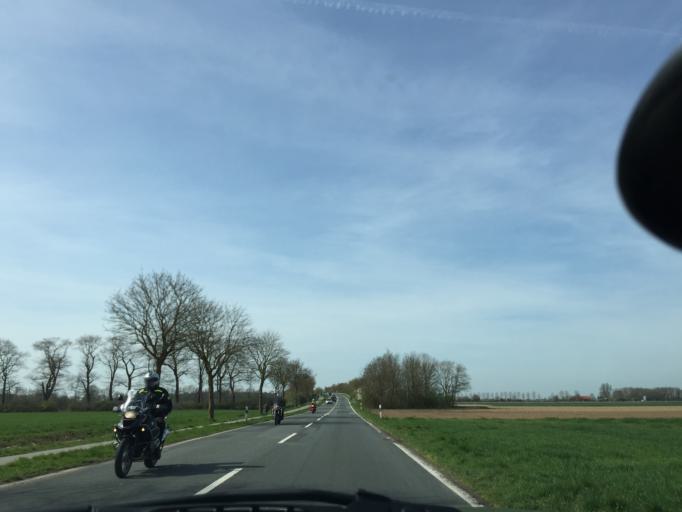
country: DE
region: North Rhine-Westphalia
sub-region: Regierungsbezirk Dusseldorf
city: Goch
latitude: 51.6688
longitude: 6.1426
